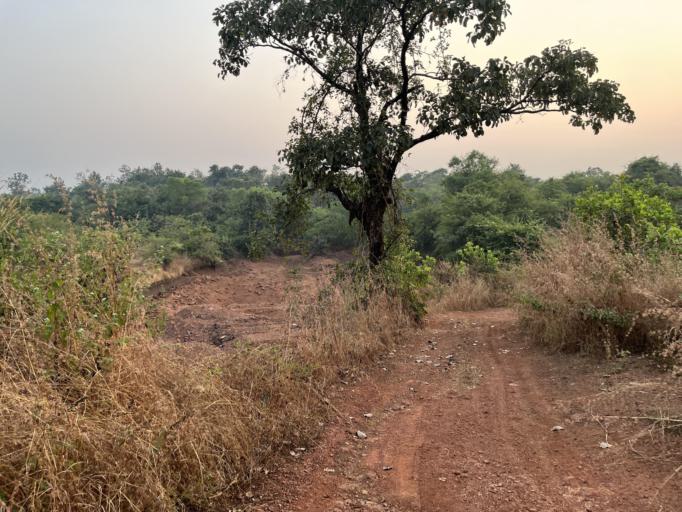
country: IN
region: Goa
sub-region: North Goa
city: Pernem
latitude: 15.6999
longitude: 73.8343
